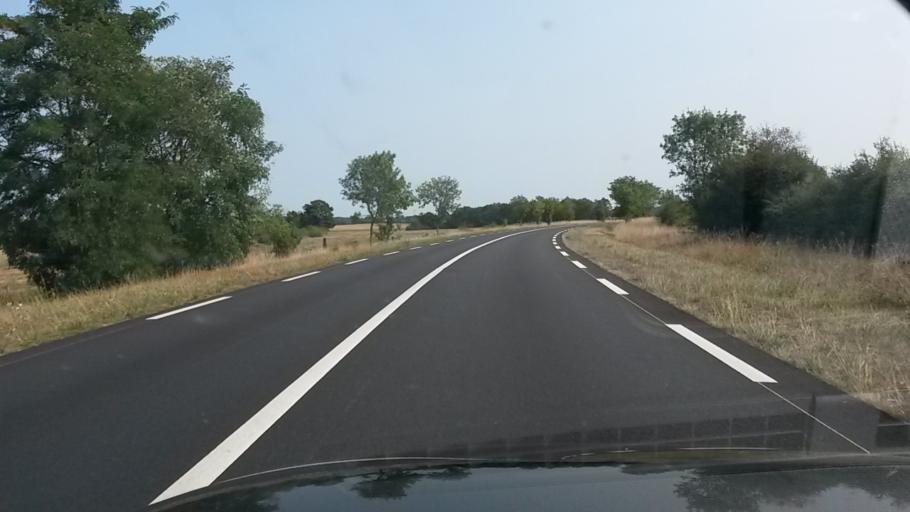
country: FR
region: Pays de la Loire
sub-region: Departement de la Loire-Atlantique
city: Ancenis
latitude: 47.3905
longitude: -1.1757
